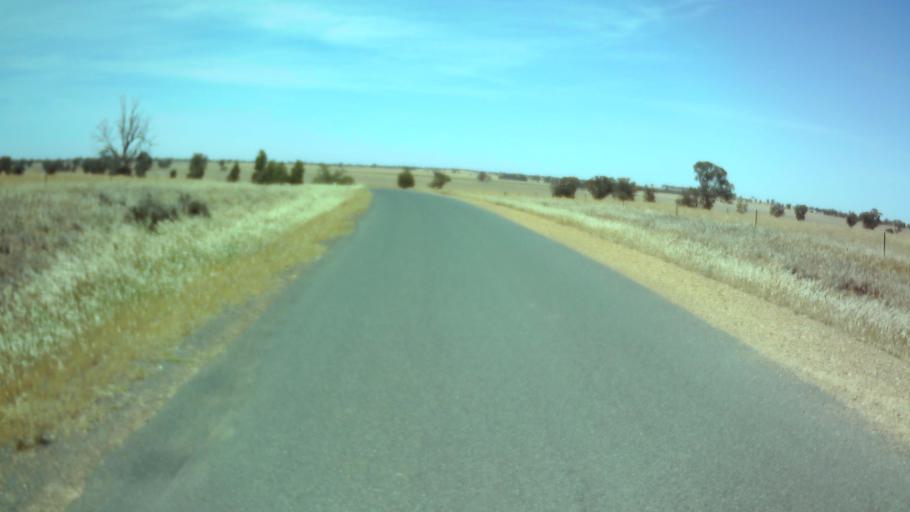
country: AU
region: New South Wales
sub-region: Weddin
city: Grenfell
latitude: -33.8570
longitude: 147.9301
